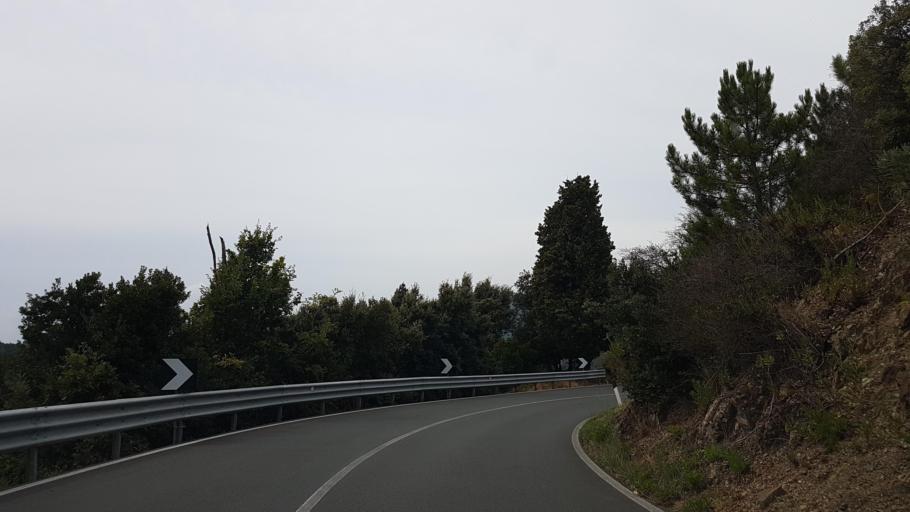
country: IT
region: Liguria
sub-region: Provincia di Genova
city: Casarza Ligure
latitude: 44.2601
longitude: 9.4456
